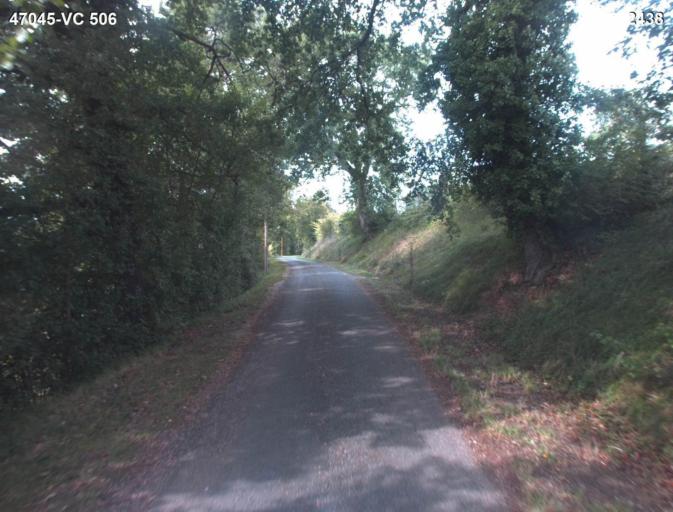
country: FR
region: Aquitaine
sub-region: Departement du Lot-et-Garonne
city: Nerac
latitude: 44.1211
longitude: 0.3934
